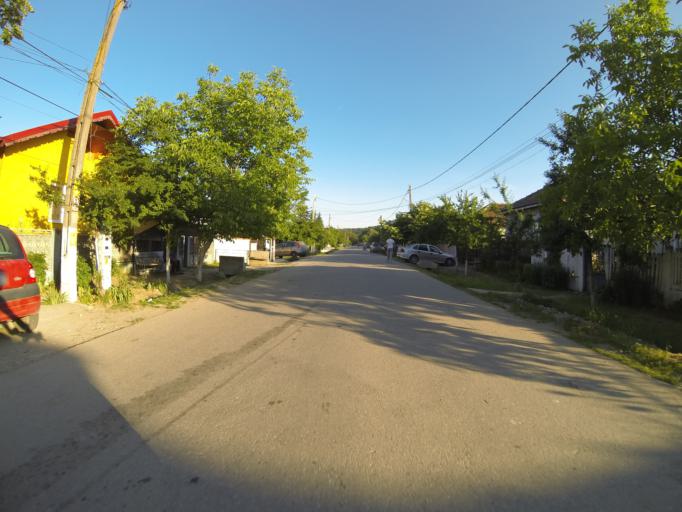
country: RO
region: Dolj
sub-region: Comuna Tuglui
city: Tuglui
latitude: 44.1792
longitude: 23.8154
